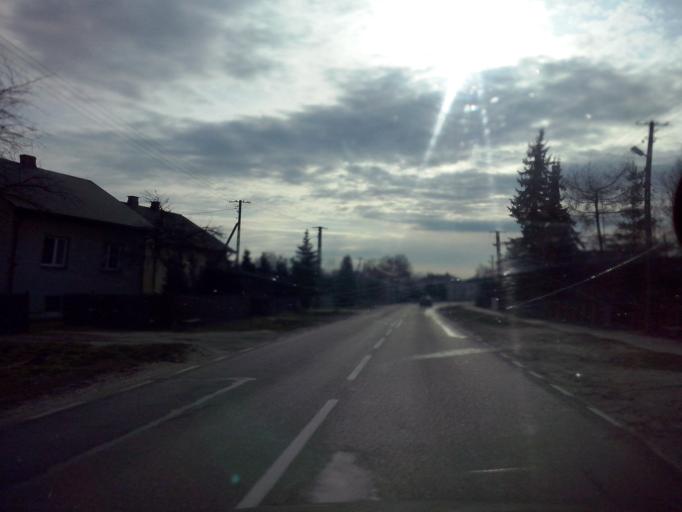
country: PL
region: Lublin Voivodeship
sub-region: Powiat bilgorajski
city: Bilgoraj
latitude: 50.4999
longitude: 22.6442
